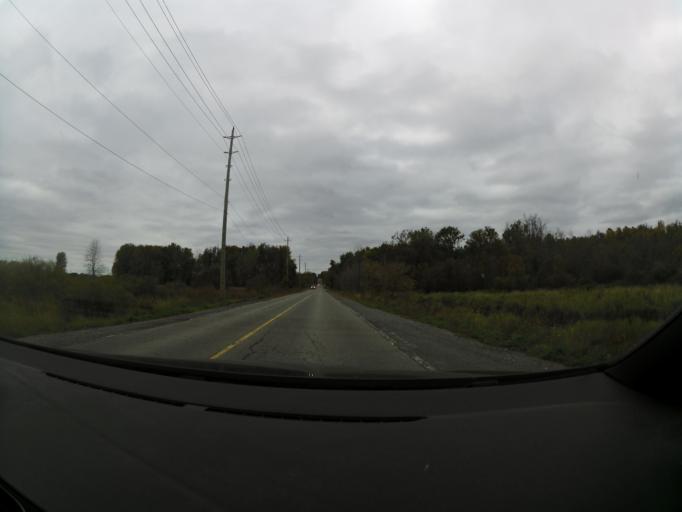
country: CA
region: Ontario
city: Bells Corners
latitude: 45.3250
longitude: -75.9653
